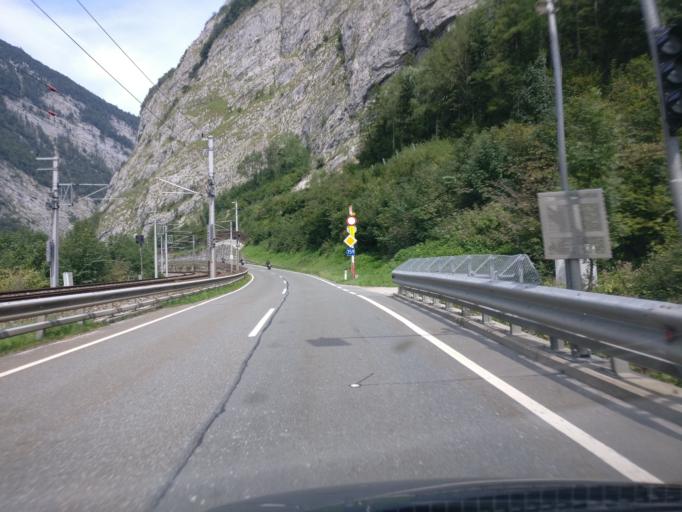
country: AT
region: Salzburg
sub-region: Politischer Bezirk Hallein
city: Golling an der Salzach
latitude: 47.5505
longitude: 13.1702
